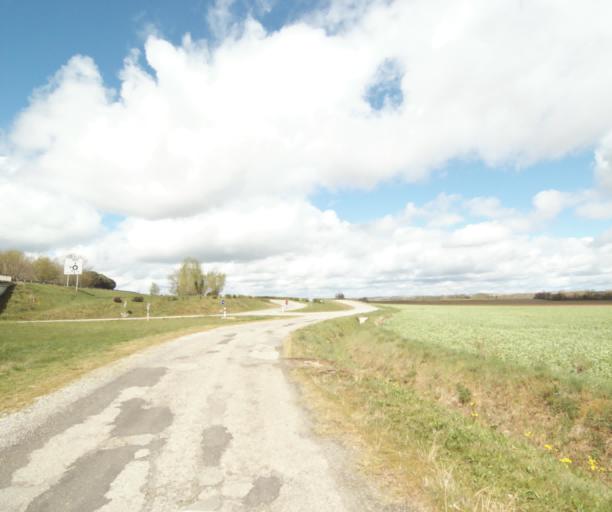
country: FR
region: Midi-Pyrenees
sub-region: Departement de l'Ariege
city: Saverdun
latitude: 43.2508
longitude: 1.5677
